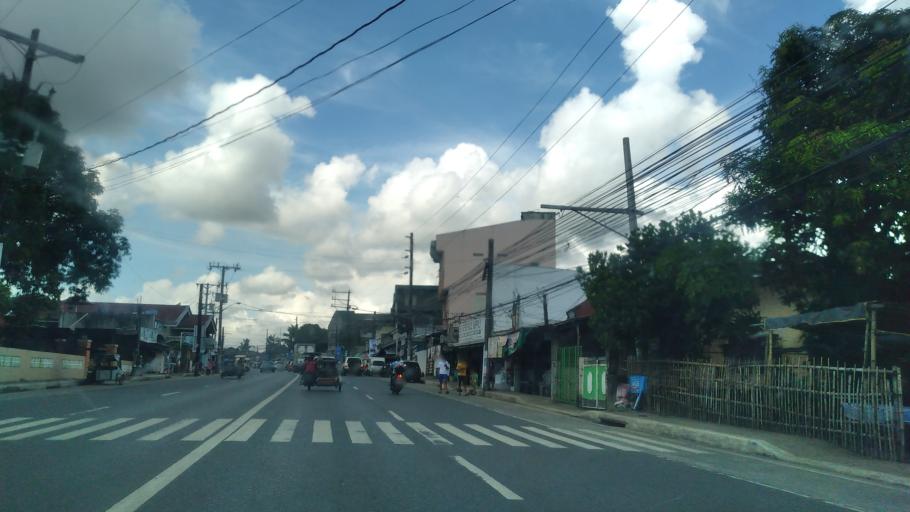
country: PH
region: Calabarzon
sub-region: Province of Quezon
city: Isabang
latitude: 13.9483
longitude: 121.5846
